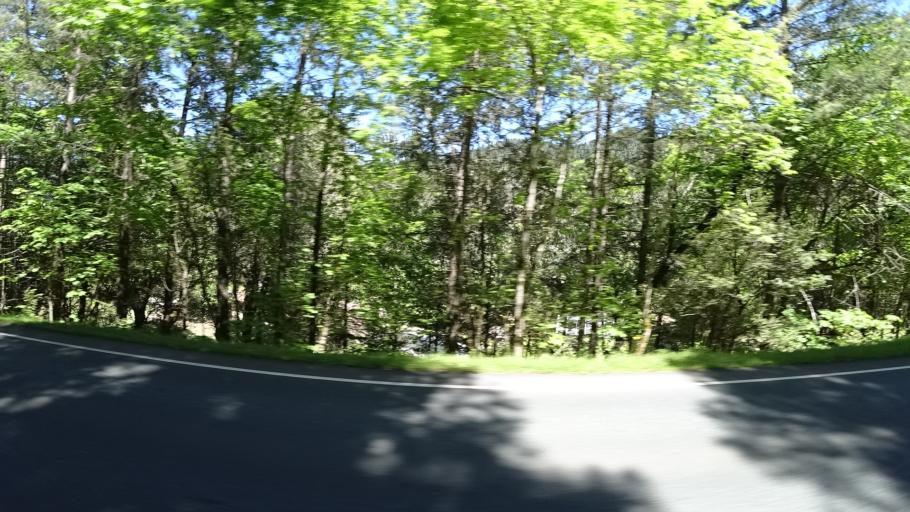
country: US
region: California
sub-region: Humboldt County
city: Willow Creek
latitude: 40.8663
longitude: -123.5192
